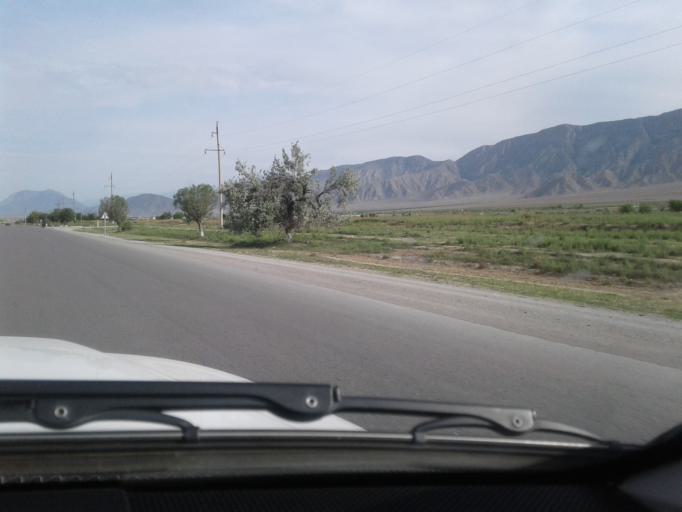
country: TM
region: Ahal
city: Arcabil
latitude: 38.1939
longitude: 57.8367
